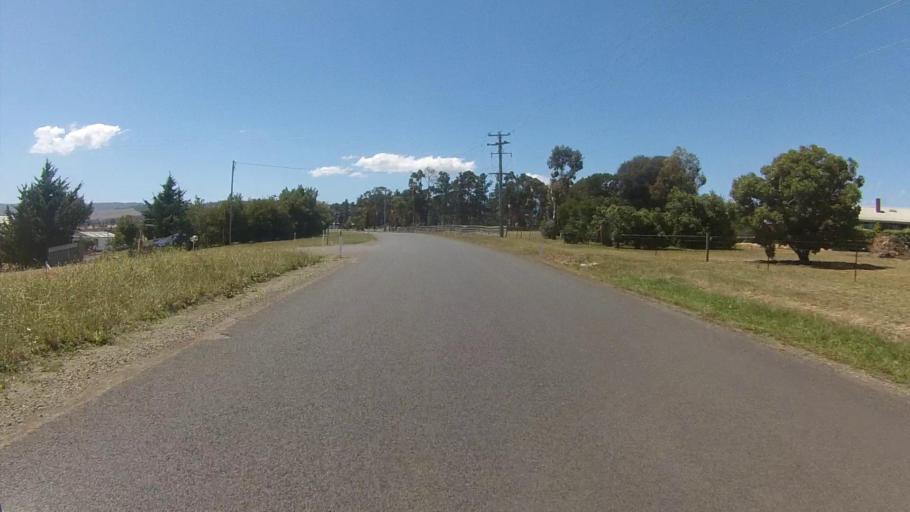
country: AU
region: Tasmania
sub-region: Sorell
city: Sorell
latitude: -42.7804
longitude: 147.5779
